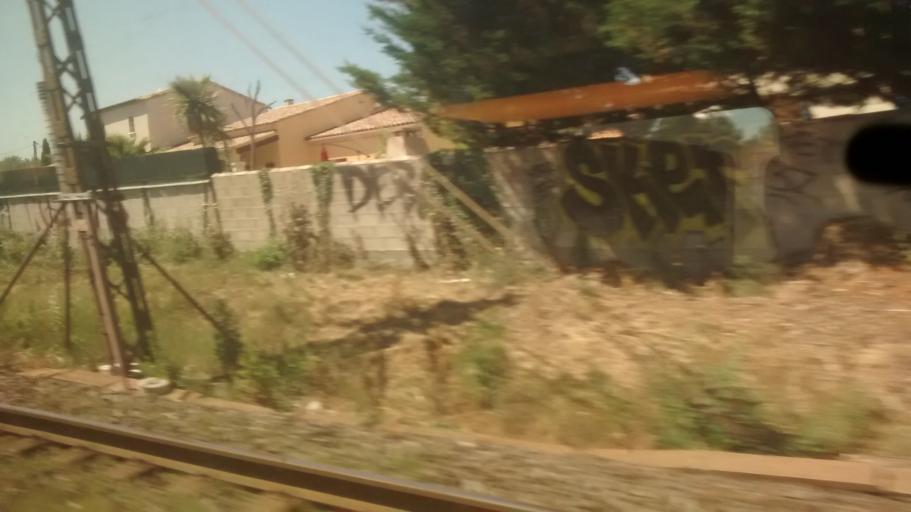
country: FR
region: Languedoc-Roussillon
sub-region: Departement du Gard
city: Vergeze
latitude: 43.7414
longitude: 4.2298
